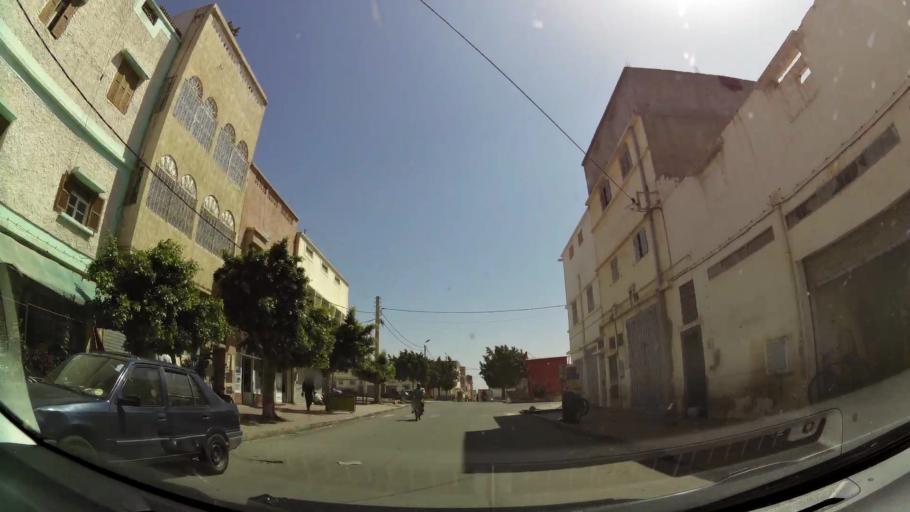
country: MA
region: Souss-Massa-Draa
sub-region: Inezgane-Ait Mellou
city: Inezgane
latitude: 30.3507
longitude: -9.5352
